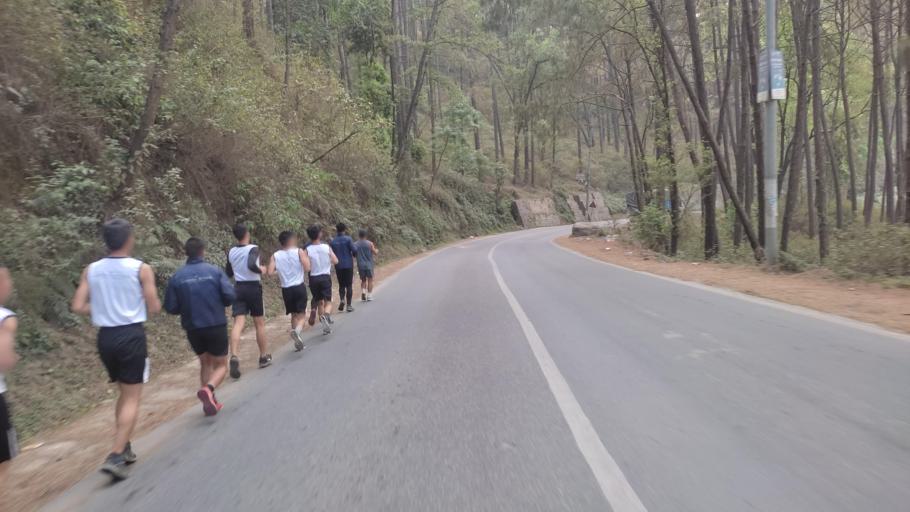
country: NP
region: Central Region
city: Kirtipur
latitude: 27.6690
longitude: 85.2922
